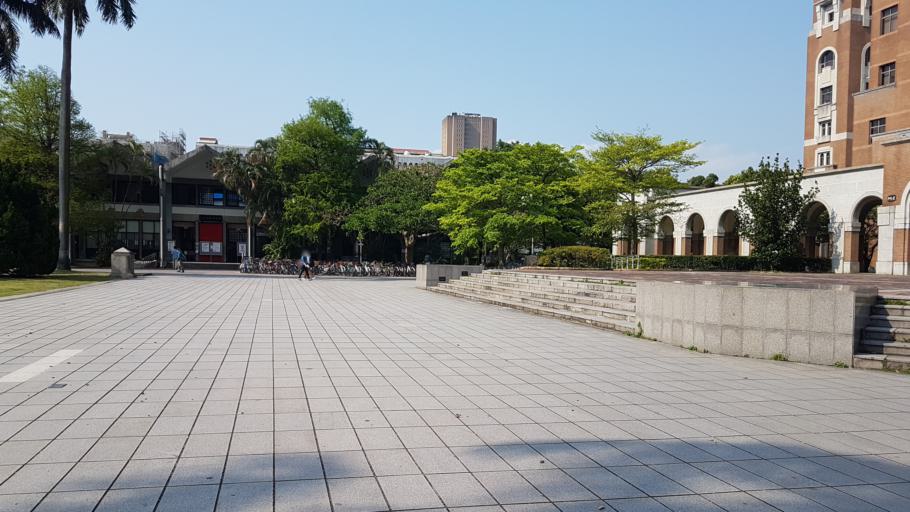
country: TW
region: Taipei
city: Taipei
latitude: 25.0172
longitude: 121.5402
